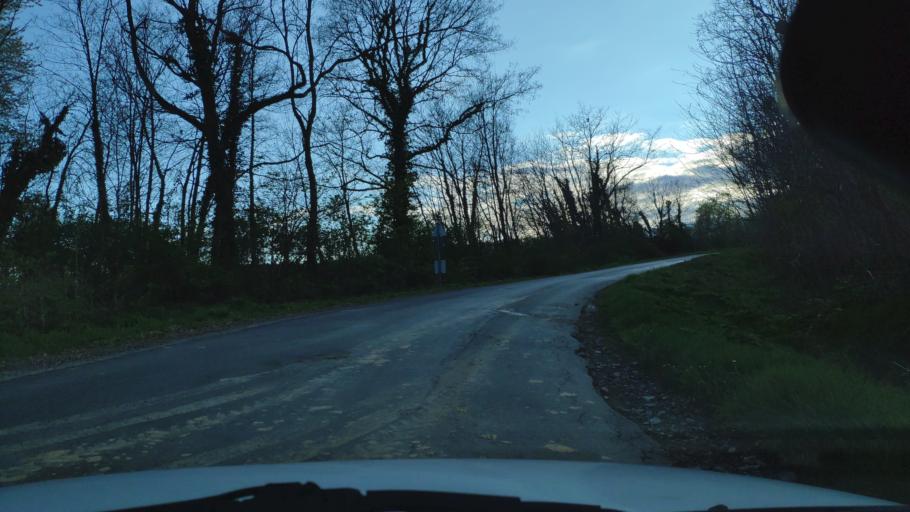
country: HU
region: Zala
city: Nagykanizsa
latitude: 46.4205
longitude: 17.1055
